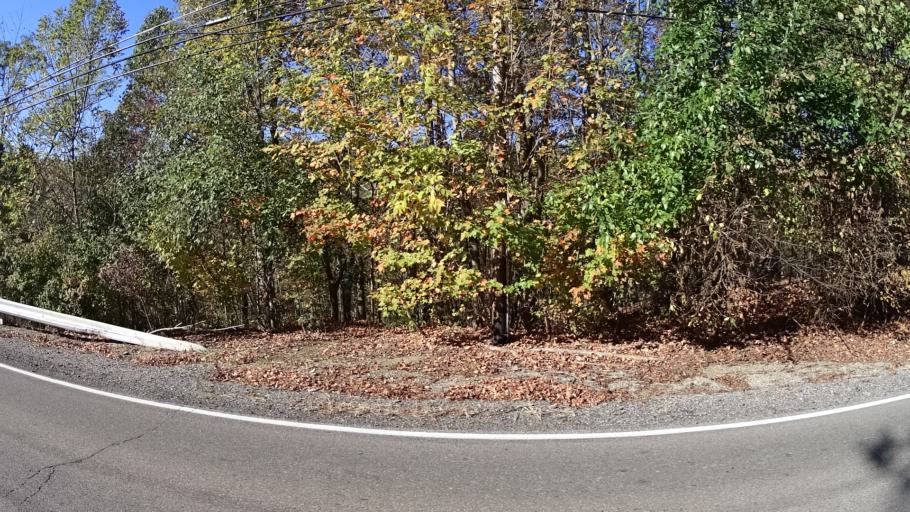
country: US
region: Ohio
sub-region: Lorain County
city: South Amherst
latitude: 41.3656
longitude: -82.2392
